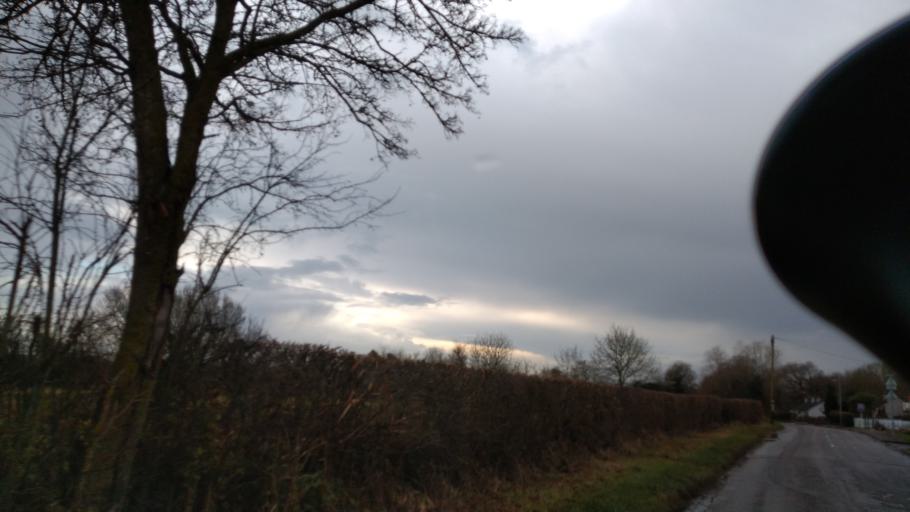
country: GB
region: England
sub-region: Borough of Swindon
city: Highworth
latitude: 51.5939
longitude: -1.7251
